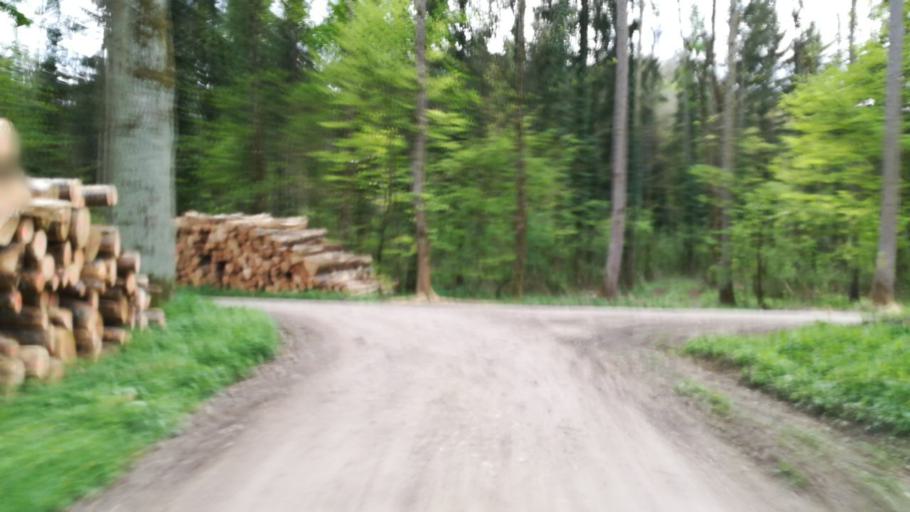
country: DE
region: Baden-Wuerttemberg
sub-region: Freiburg Region
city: Singen
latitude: 47.7521
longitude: 8.8104
